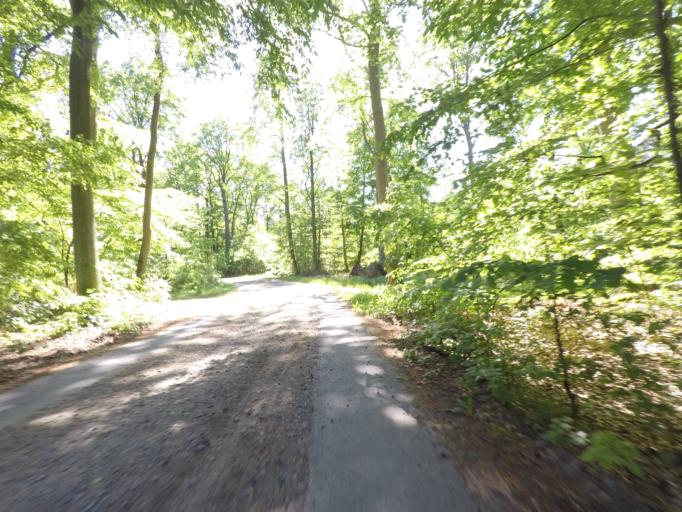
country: DE
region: Brandenburg
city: Eberswalde
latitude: 52.8169
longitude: 13.7783
